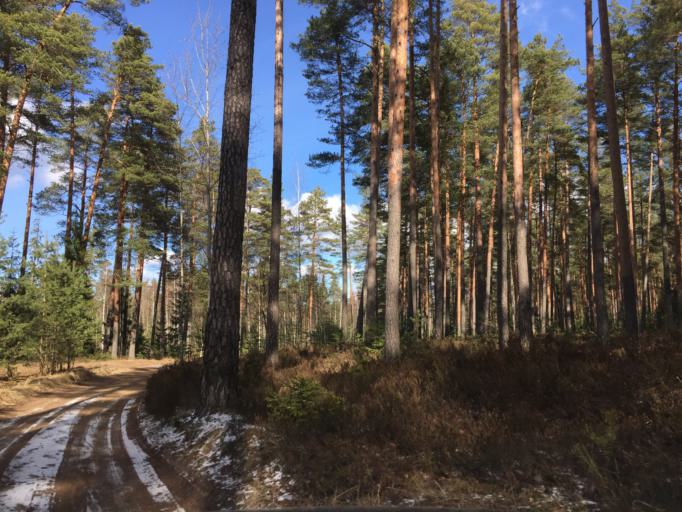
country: LV
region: Garkalne
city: Garkalne
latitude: 56.9665
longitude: 24.4255
